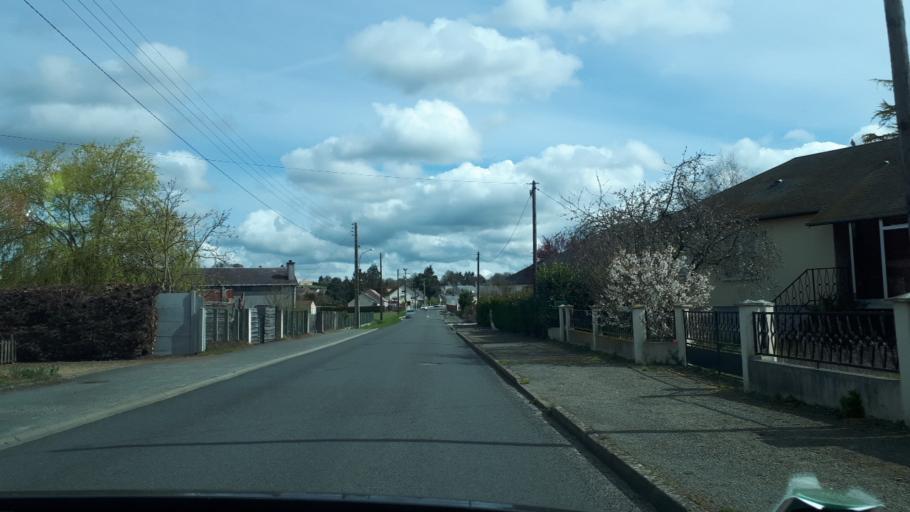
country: FR
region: Pays de la Loire
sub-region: Departement de la Sarthe
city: Brette-les-Pins
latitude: 47.8678
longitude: 0.3267
